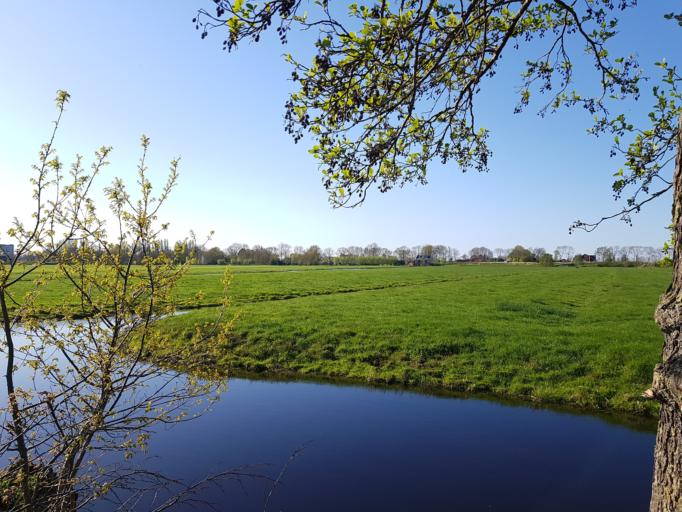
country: NL
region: South Holland
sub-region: Gemeente Vlist
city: Vlist
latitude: 52.0111
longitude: 4.8269
